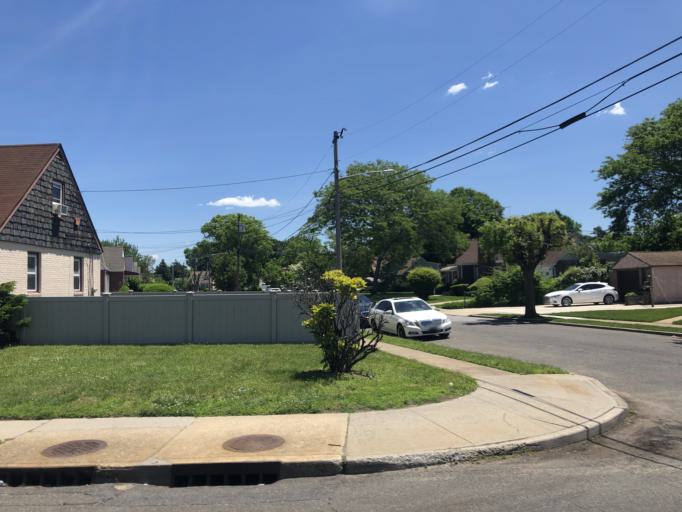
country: US
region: New York
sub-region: Nassau County
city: Uniondale
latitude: 40.6968
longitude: -73.5946
